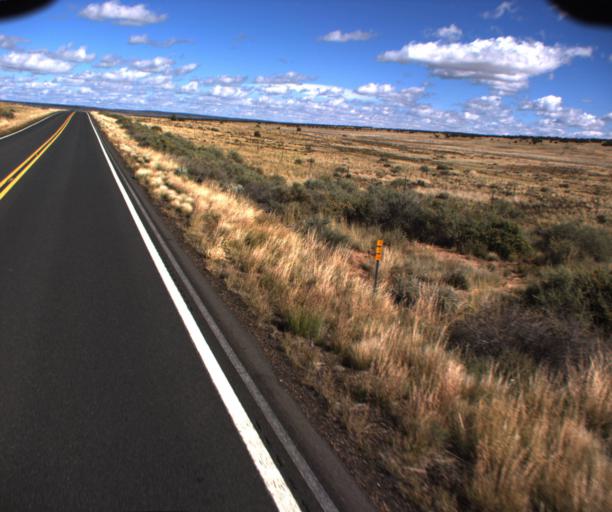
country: US
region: Arizona
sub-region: Apache County
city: Houck
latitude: 34.9717
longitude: -109.2272
